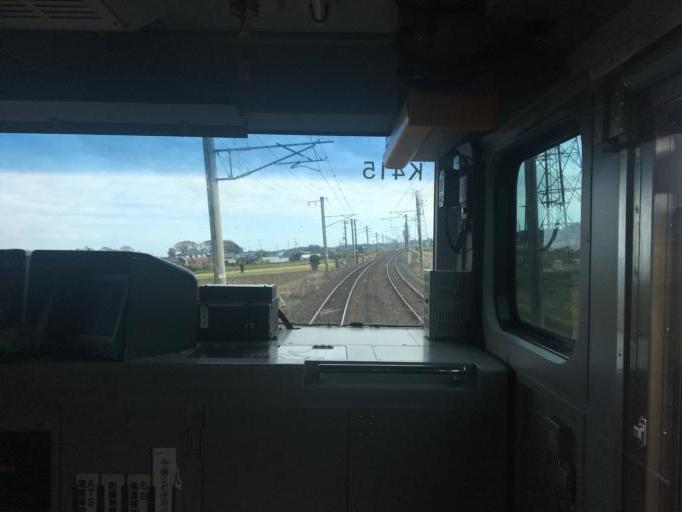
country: JP
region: Ibaraki
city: Tomobe
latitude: 36.3737
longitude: 140.3642
